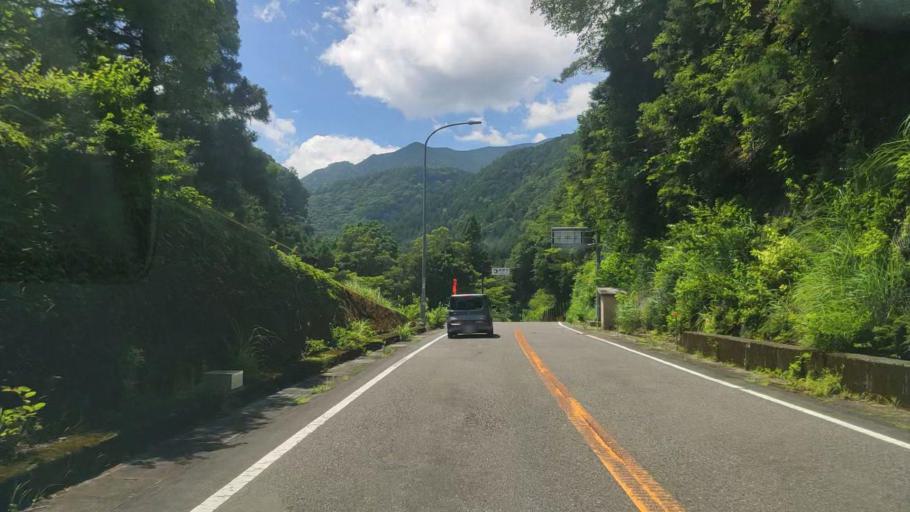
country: JP
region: Mie
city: Owase
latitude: 33.9919
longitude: 136.1209
